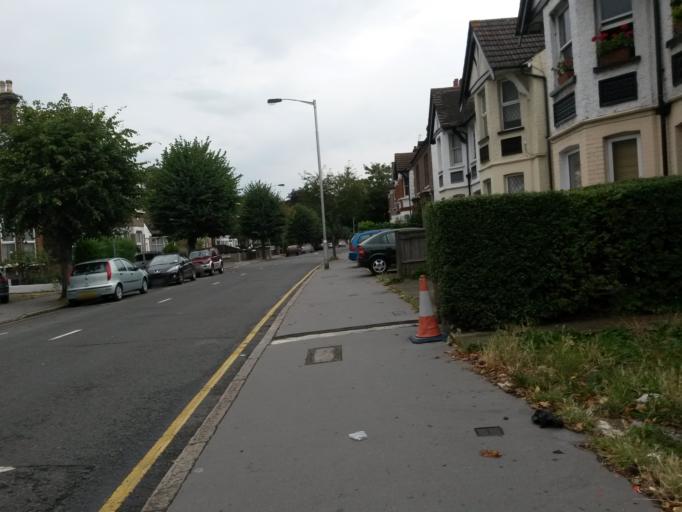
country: GB
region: England
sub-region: Greater London
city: Croydon
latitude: 51.3806
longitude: -0.1021
